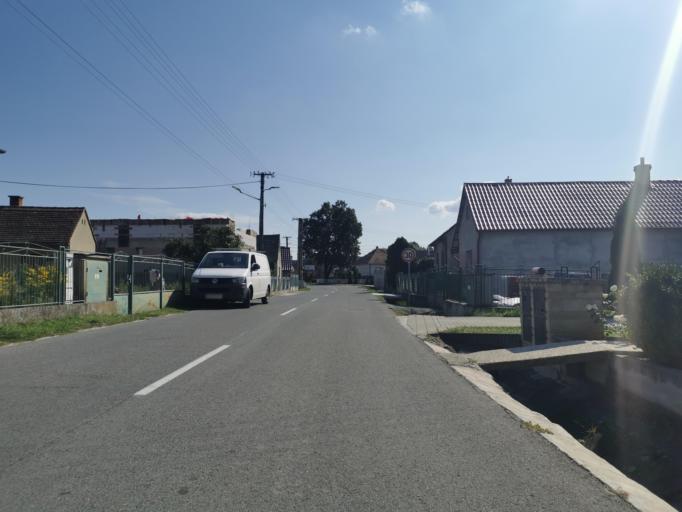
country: SK
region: Trnavsky
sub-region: Okres Senica
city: Senica
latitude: 48.6562
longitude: 17.2660
